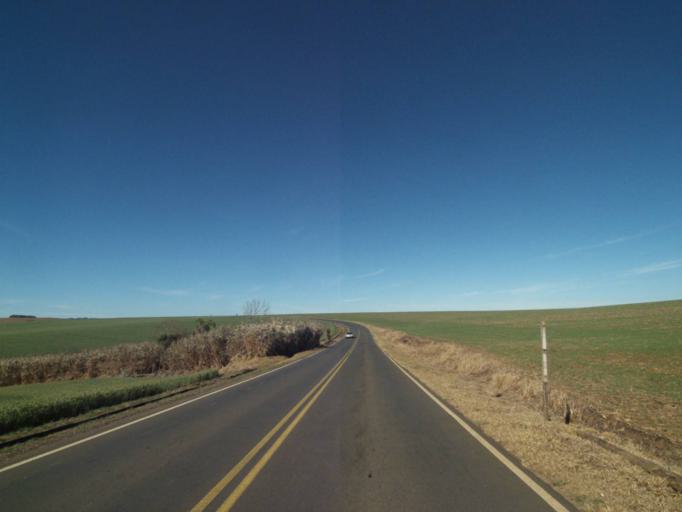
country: BR
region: Parana
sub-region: Tibagi
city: Tibagi
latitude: -24.5617
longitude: -50.2904
